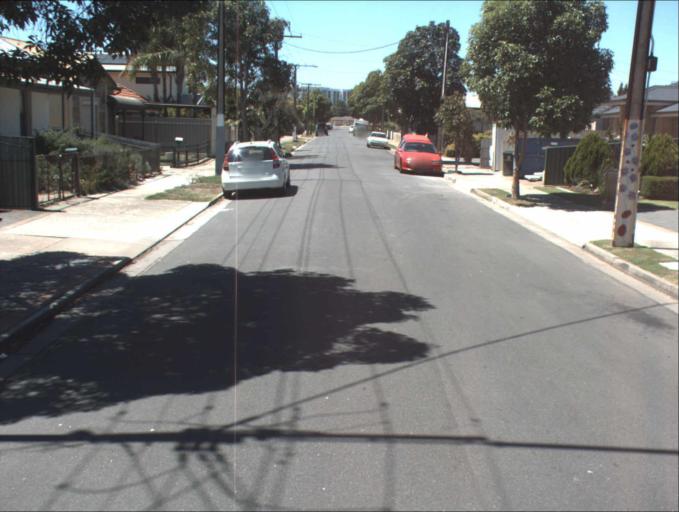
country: AU
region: South Australia
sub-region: Port Adelaide Enfield
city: Birkenhead
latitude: -34.8435
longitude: 138.4880
